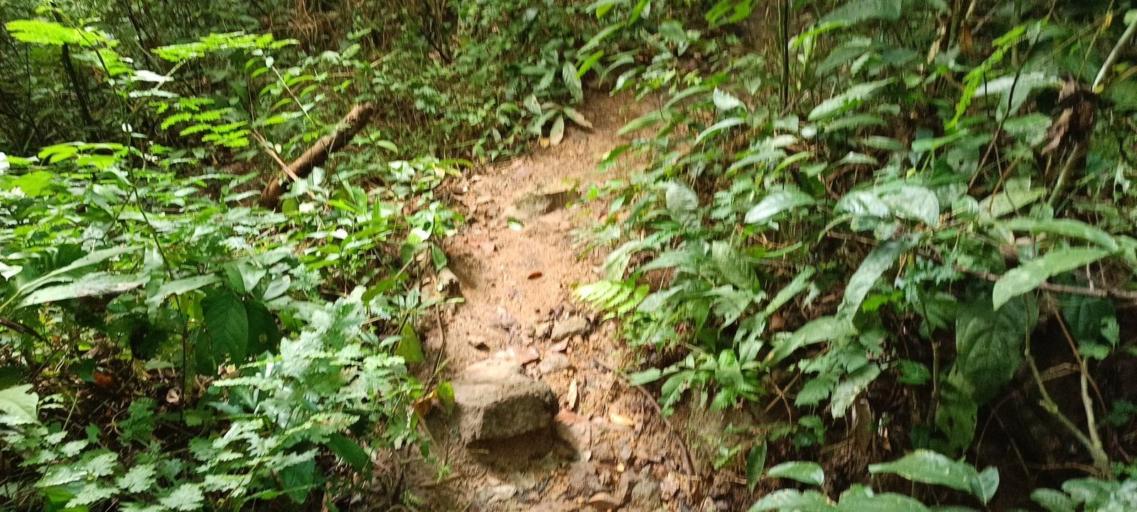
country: MY
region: Penang
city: Bukit Mertajam
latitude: 5.3640
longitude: 100.4940
